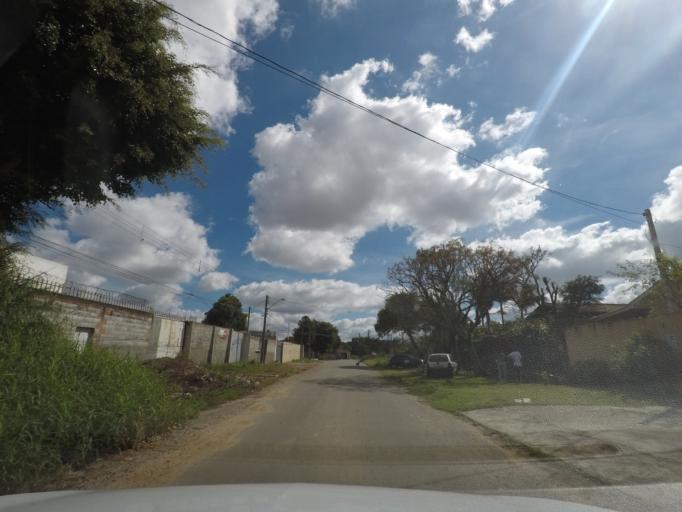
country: BR
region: Parana
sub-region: Sao Jose Dos Pinhais
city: Sao Jose dos Pinhais
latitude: -25.4973
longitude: -49.2249
